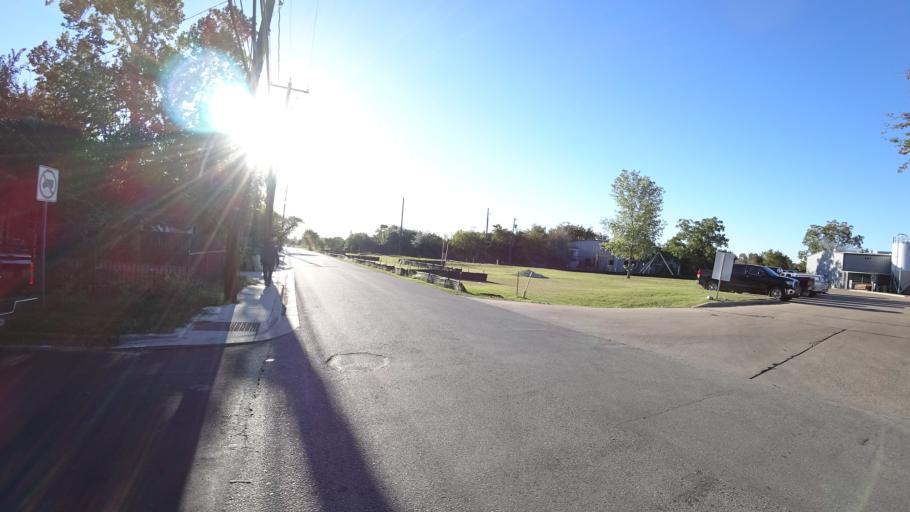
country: US
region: Texas
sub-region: Travis County
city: Austin
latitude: 30.2237
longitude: -97.7697
